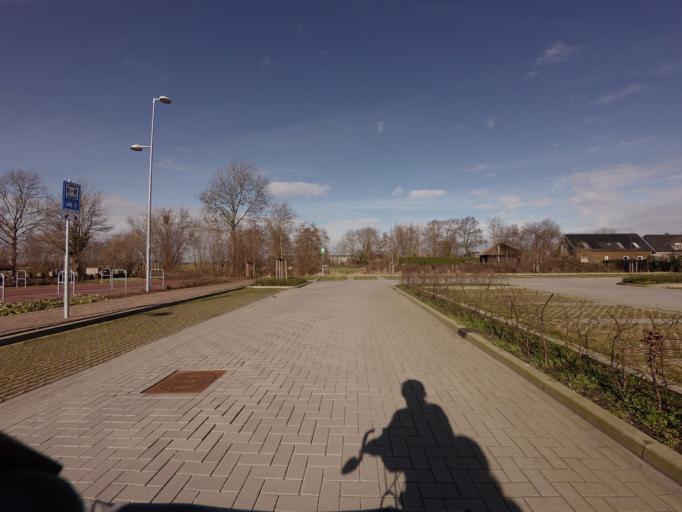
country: NL
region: Utrecht
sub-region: Gemeente Woerden
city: Woerden
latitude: 52.1153
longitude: 4.8925
